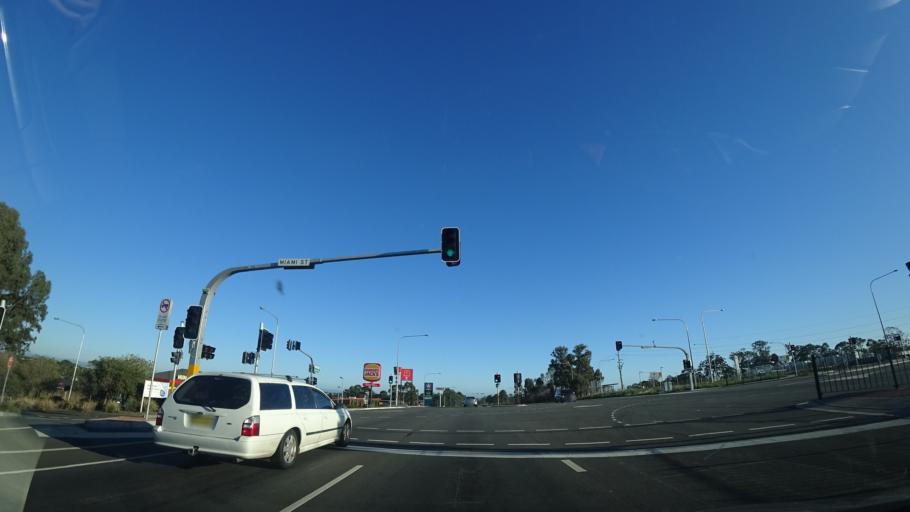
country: AU
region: New South Wales
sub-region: Blacktown
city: Stanhope Gardens
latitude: -33.7256
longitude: 150.9401
